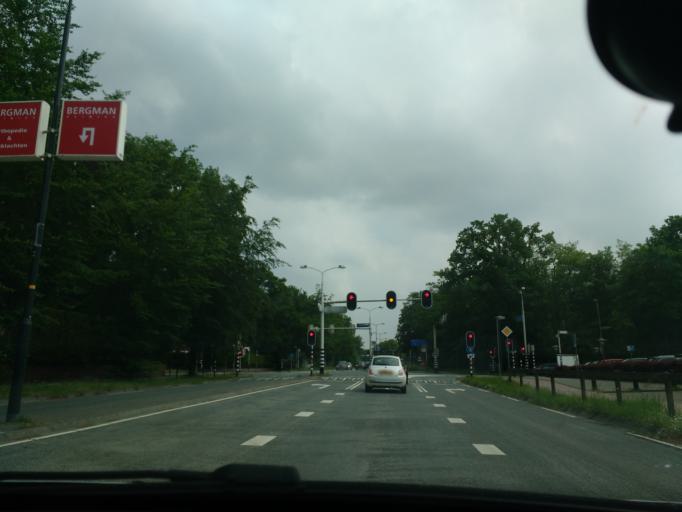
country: NL
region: North Holland
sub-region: Gemeente Bussum
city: Bussum
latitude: 52.2834
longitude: 5.1789
